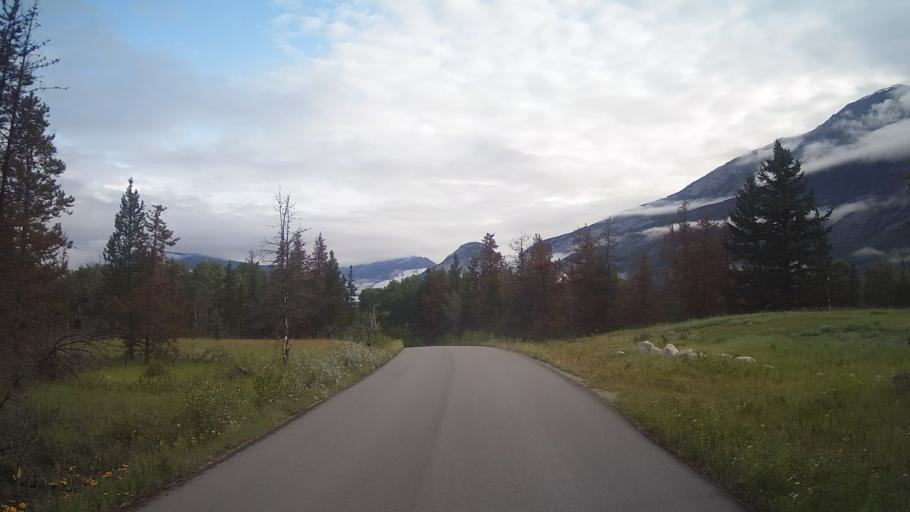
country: CA
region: Alberta
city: Jasper Park Lodge
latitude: 52.9686
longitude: -118.0591
